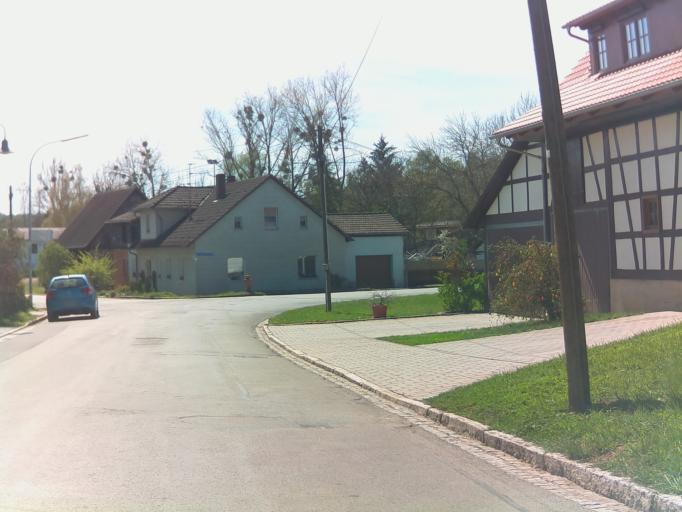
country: DE
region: Thuringia
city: Veilsdorf
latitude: 50.3063
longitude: 10.8027
